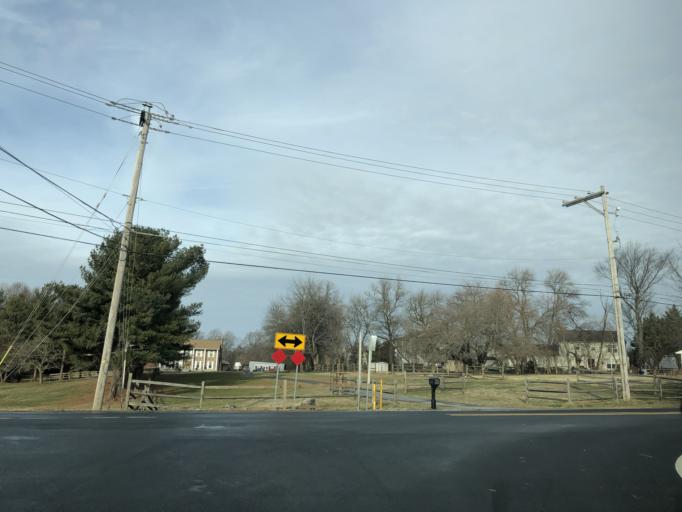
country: US
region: Delaware
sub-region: New Castle County
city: Townsend
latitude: 39.4398
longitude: -75.6438
